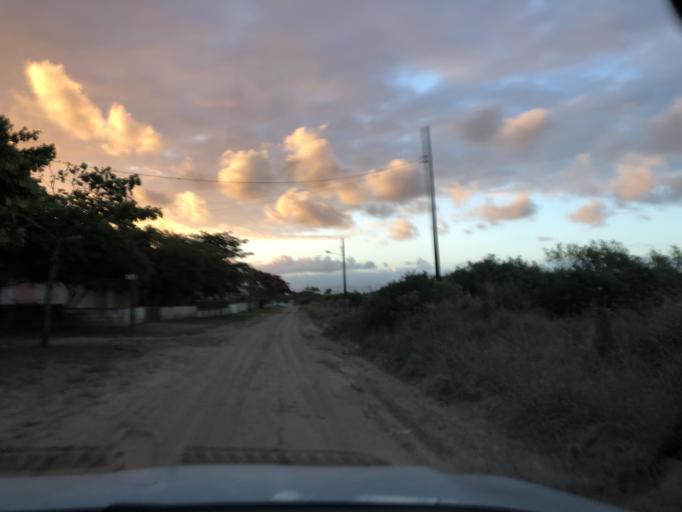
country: BR
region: Santa Catarina
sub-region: Sao Francisco Do Sul
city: Sao Francisco do Sul
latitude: -26.2371
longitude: -48.5091
